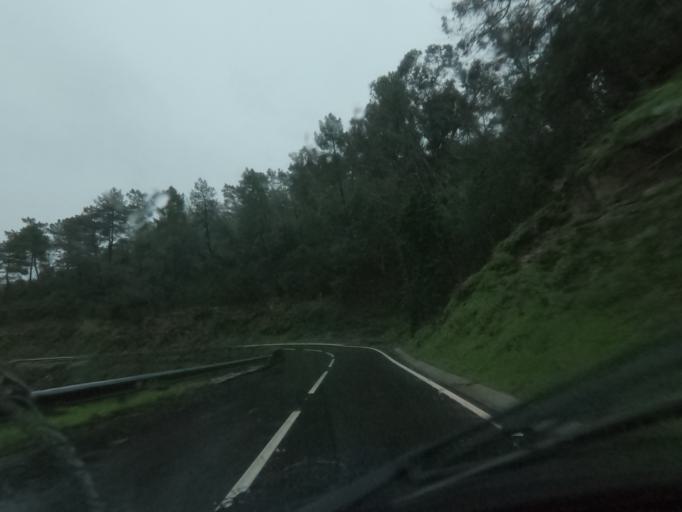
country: PT
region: Vila Real
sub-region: Sabrosa
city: Vilela
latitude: 41.1980
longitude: -7.5548
